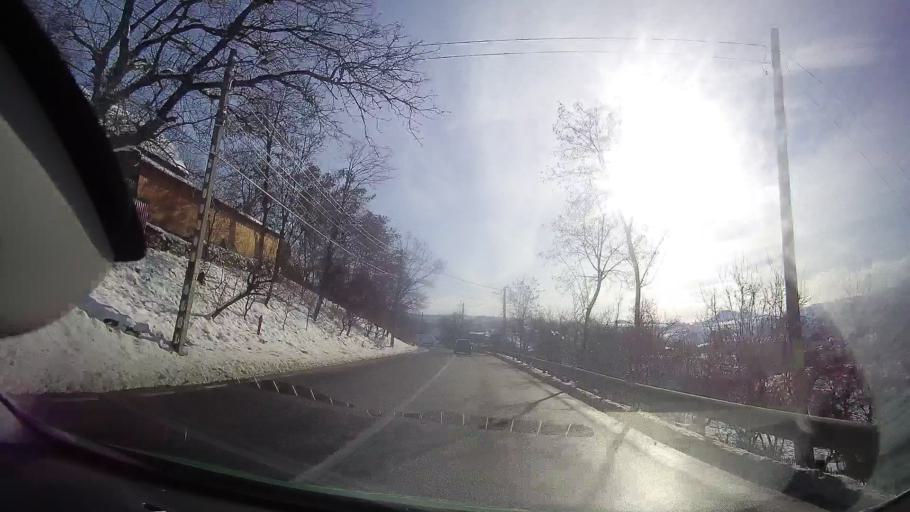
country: RO
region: Neamt
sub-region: Comuna Baltatesti
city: Baltatesti
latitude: 47.1159
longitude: 26.3126
